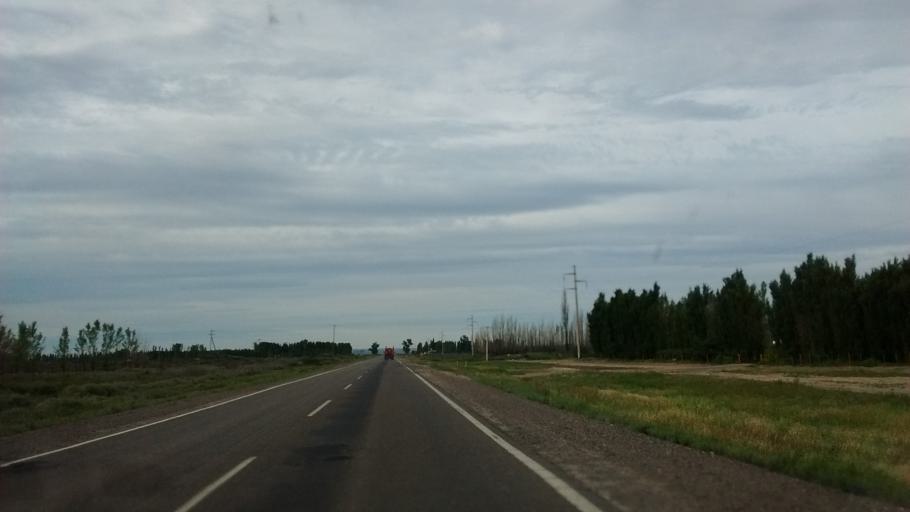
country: AR
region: Rio Negro
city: Catriel
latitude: -37.9129
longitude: -67.8689
